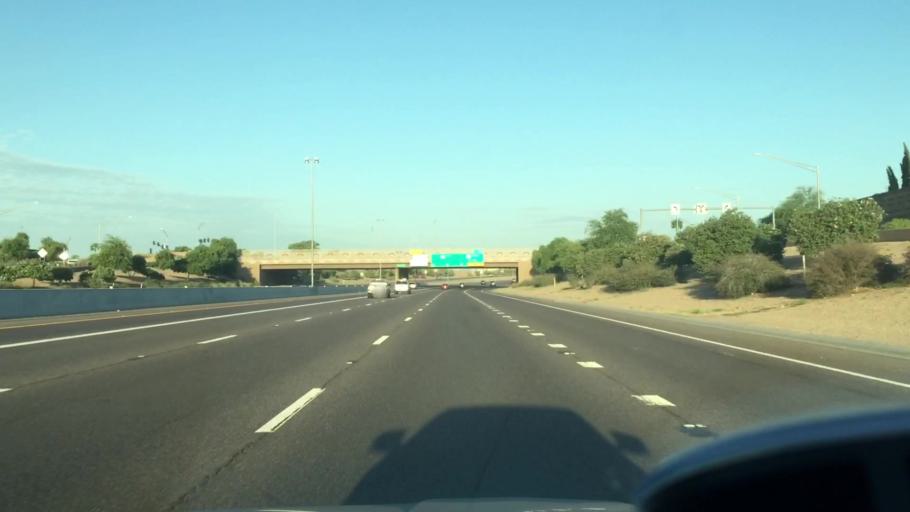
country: US
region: Arizona
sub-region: Maricopa County
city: Chandler
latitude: 33.2875
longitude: -111.8734
